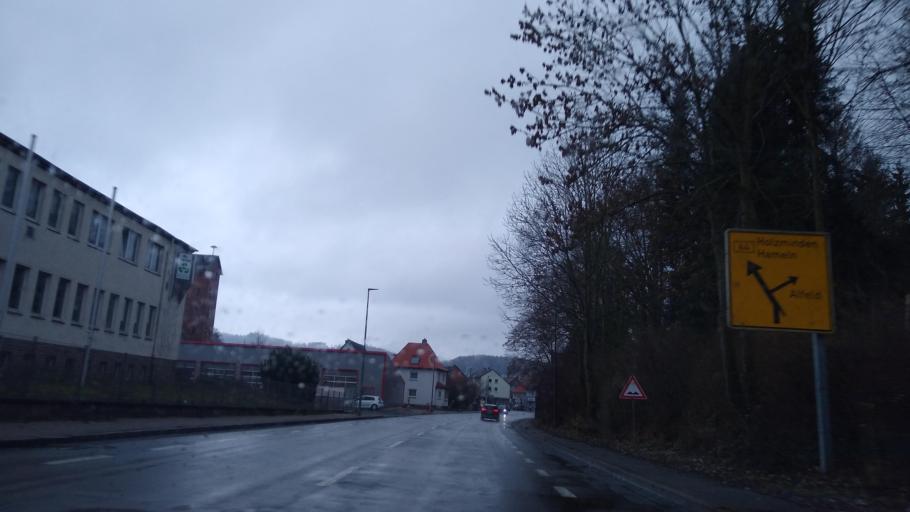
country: DE
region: Lower Saxony
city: Eschershausen
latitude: 51.9257
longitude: 9.6447
